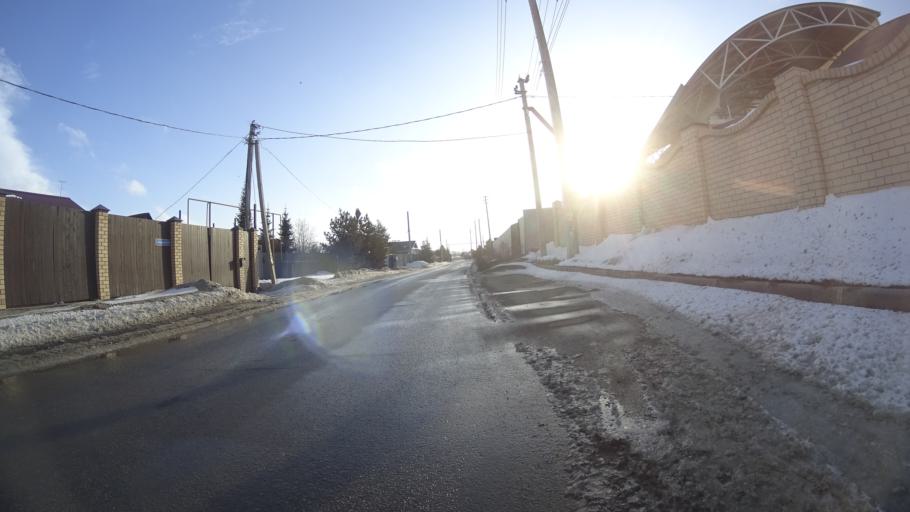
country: RU
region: Chelyabinsk
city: Sargazy
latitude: 55.1126
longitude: 61.2809
